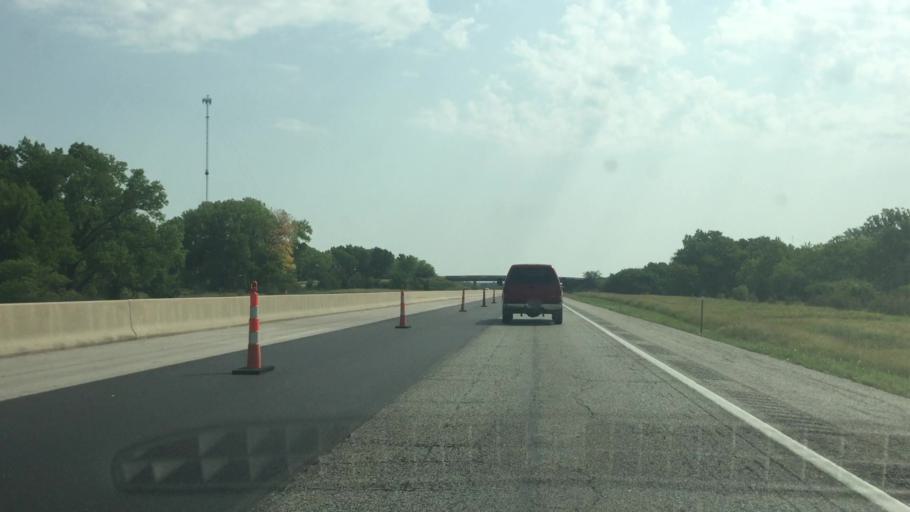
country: US
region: Kansas
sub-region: Chase County
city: Cottonwood Falls
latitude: 38.1438
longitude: -96.5170
